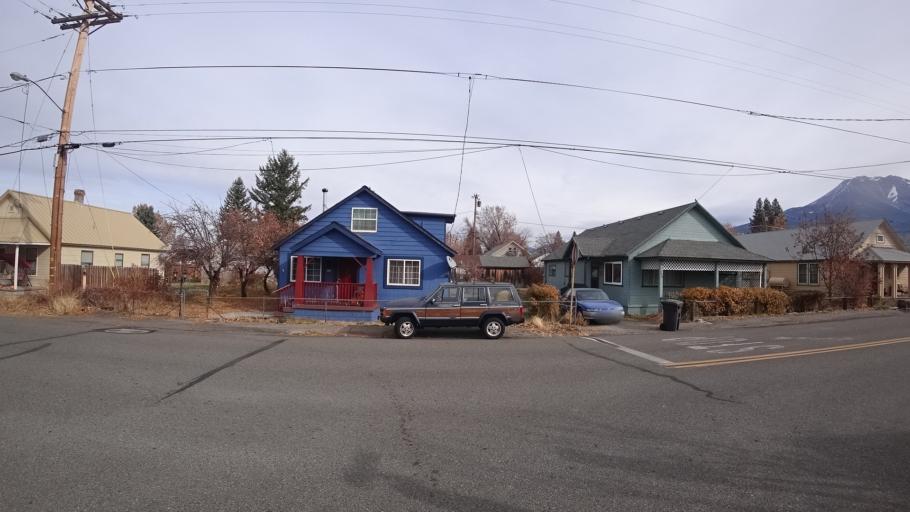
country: US
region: California
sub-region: Siskiyou County
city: Weed
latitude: 41.4288
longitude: -122.3761
